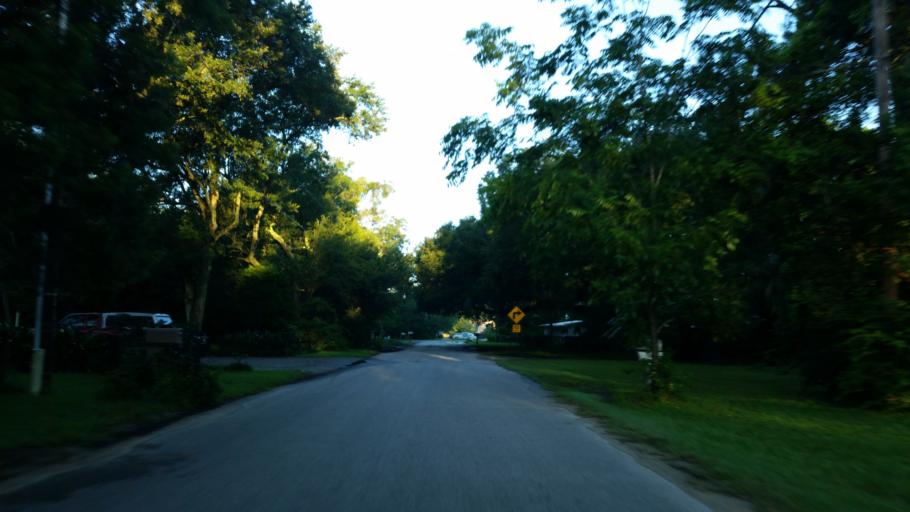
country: US
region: Florida
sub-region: Escambia County
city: Ferry Pass
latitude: 30.4982
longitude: -87.2161
